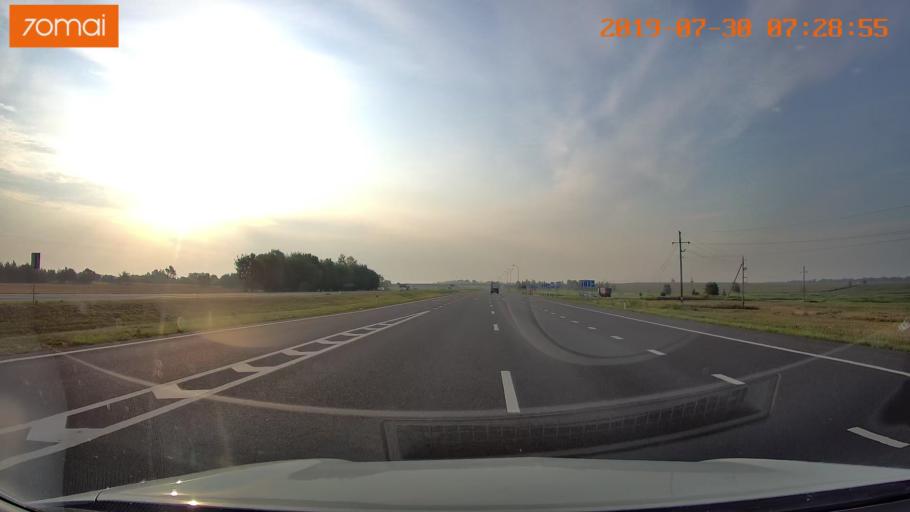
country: RU
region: Kaliningrad
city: Gvardeysk
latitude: 54.6750
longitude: 20.9269
